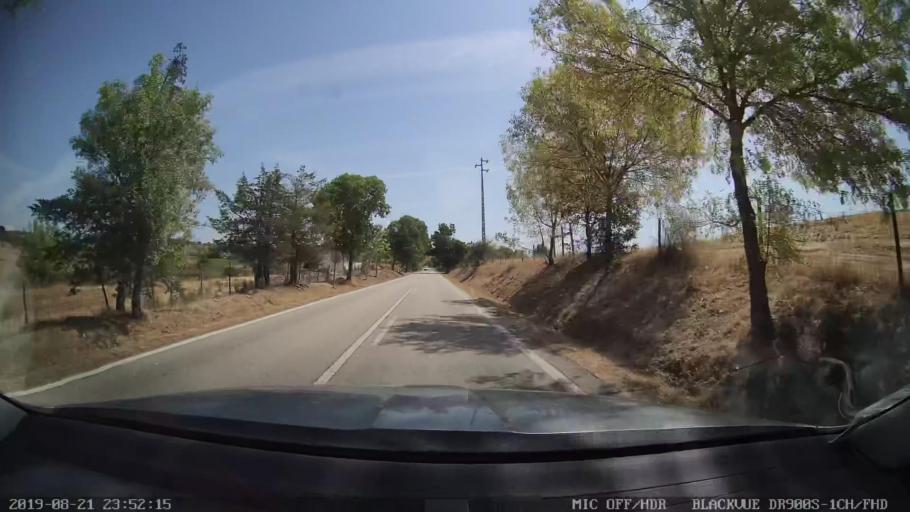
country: PT
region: Castelo Branco
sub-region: Idanha-A-Nova
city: Idanha-a-Nova
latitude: 39.9083
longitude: -7.2263
